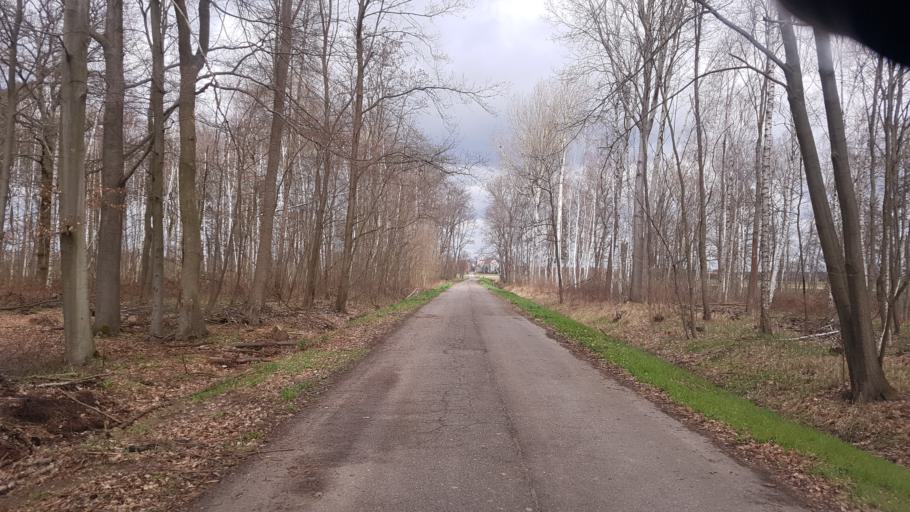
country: DE
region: Brandenburg
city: Hohenbucko
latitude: 51.6904
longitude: 13.4686
